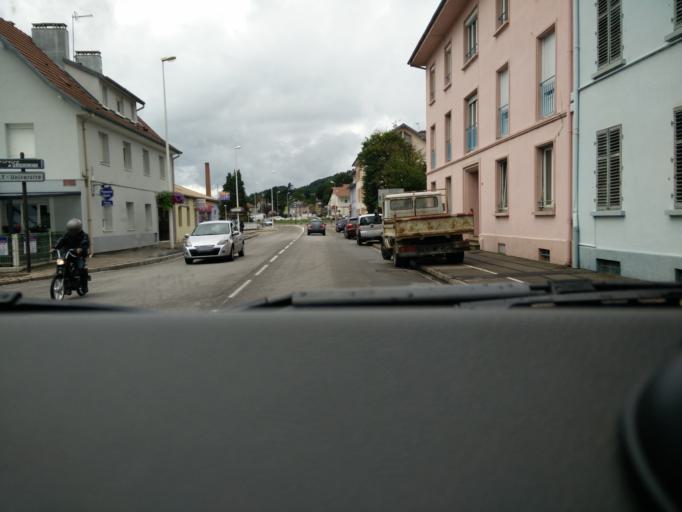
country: FR
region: Lorraine
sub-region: Departement des Vosges
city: Saint-Die-des-Vosges
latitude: 48.2903
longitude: 6.9432
